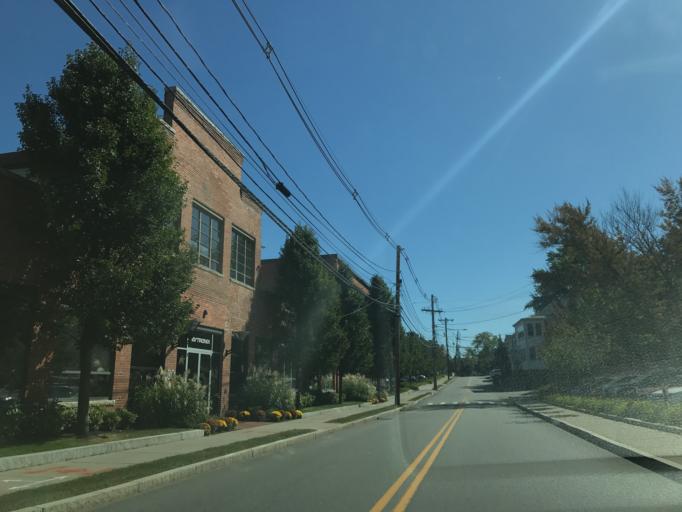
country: US
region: Massachusetts
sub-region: Middlesex County
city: Watertown
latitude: 42.3628
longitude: -71.2031
